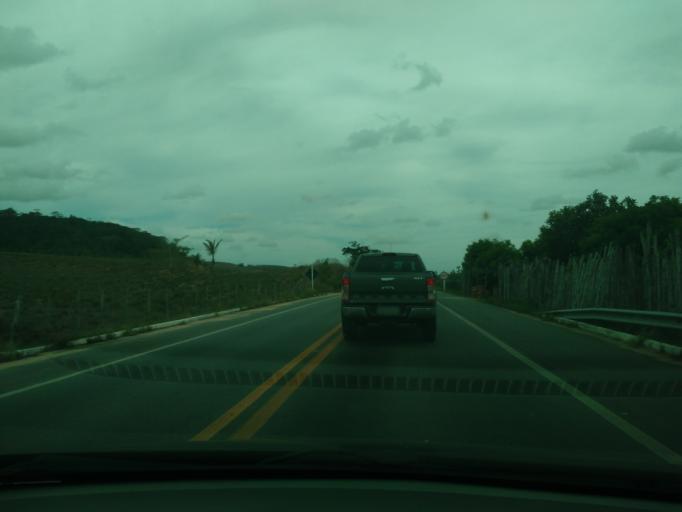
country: BR
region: Alagoas
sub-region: Murici
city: Murici
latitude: -9.3177
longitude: -35.9292
